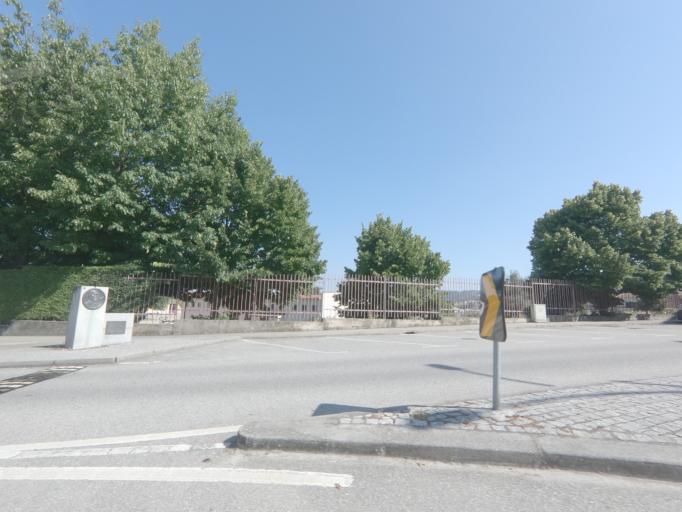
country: PT
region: Viseu
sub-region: Moimenta da Beira
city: Moimenta da Beira
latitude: 40.9851
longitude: -7.6167
